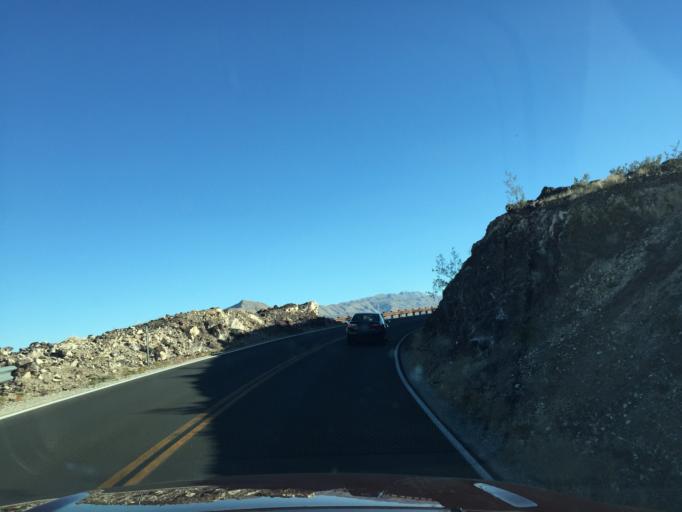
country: US
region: California
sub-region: Inyo County
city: Lone Pine
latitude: 36.3546
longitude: -117.5346
